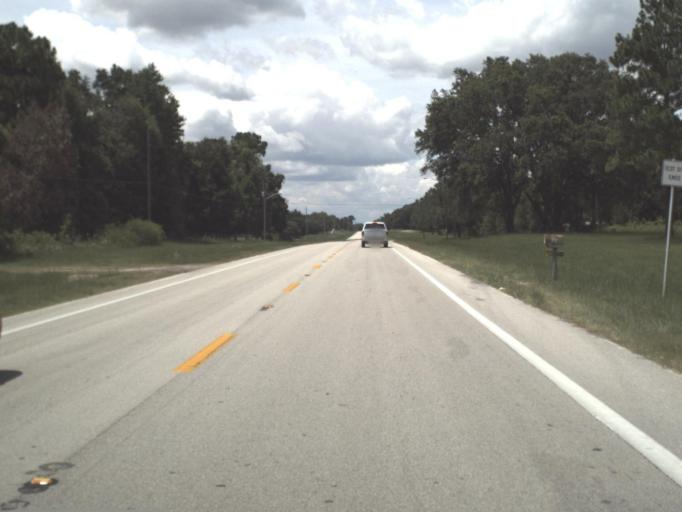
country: US
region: Florida
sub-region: Alachua County
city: Newberry
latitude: 29.6748
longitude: -82.6070
